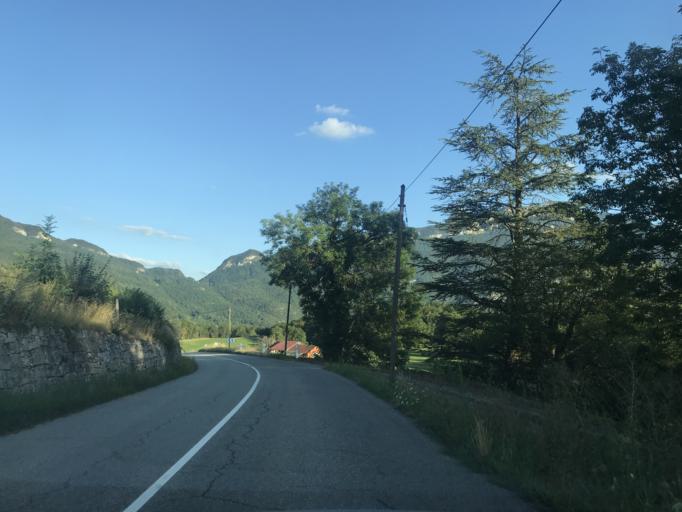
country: FR
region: Rhone-Alpes
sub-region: Departement de la Savoie
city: Yenne
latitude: 45.7165
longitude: 5.8125
